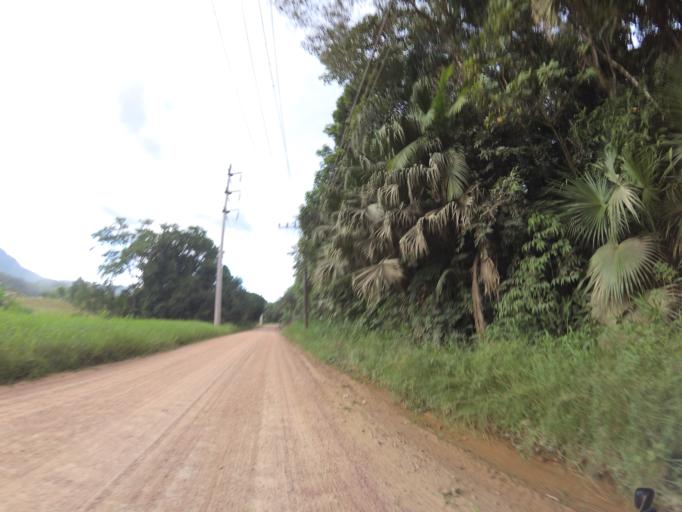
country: BR
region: Santa Catarina
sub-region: Pomerode
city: Pomerode
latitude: -26.7735
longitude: -49.1635
